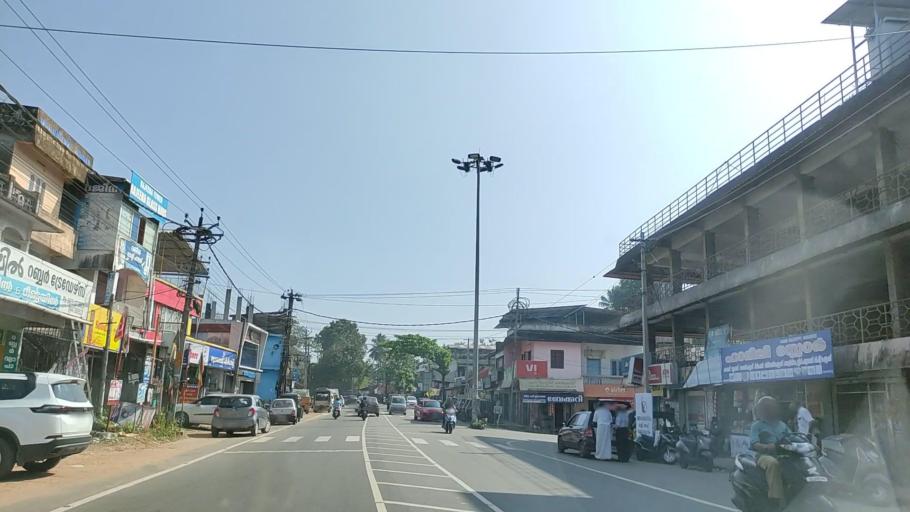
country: IN
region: Kerala
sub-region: Kollam
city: Punalur
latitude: 8.9298
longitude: 76.9314
